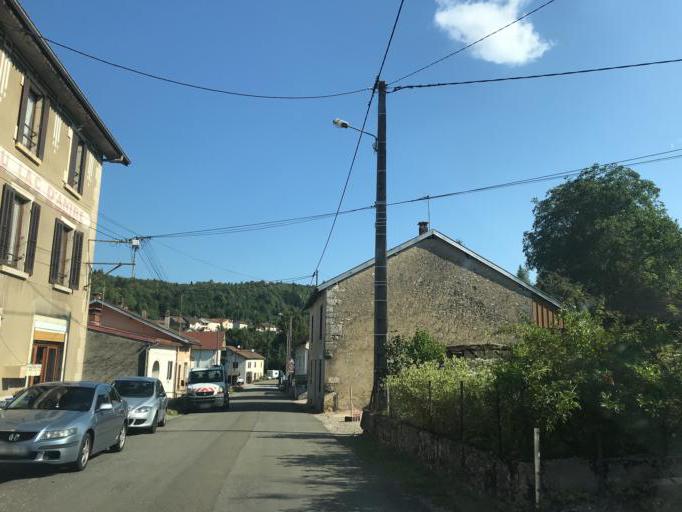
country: FR
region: Franche-Comte
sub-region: Departement du Jura
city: Moirans-en-Montagne
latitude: 46.4142
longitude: 5.7352
